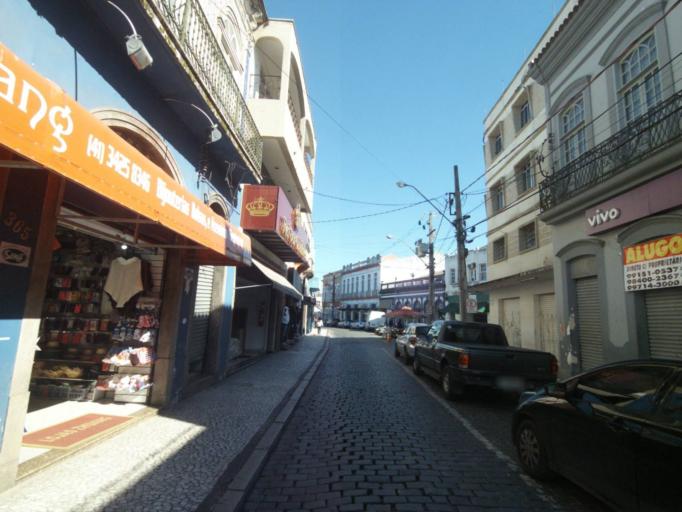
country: BR
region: Parana
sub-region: Paranagua
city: Paranagua
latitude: -25.5201
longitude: -48.5060
